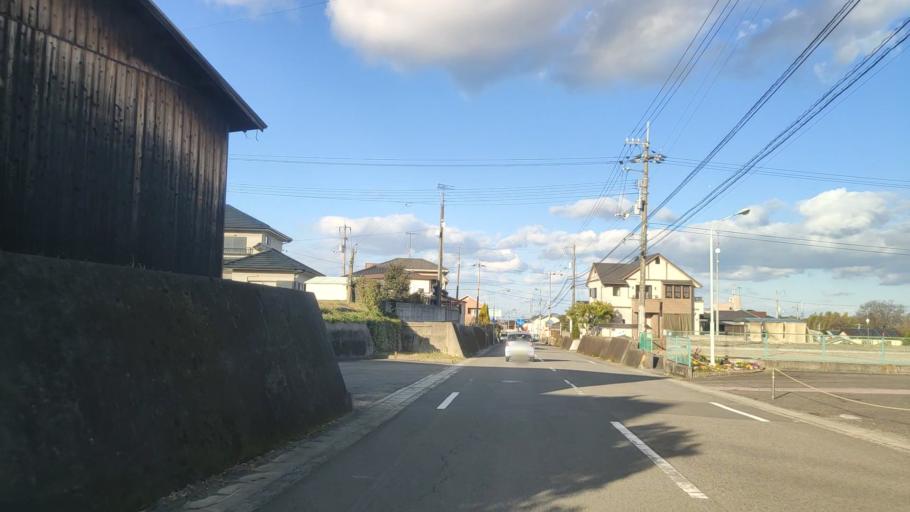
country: JP
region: Ehime
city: Saijo
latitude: 33.8913
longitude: 133.1315
